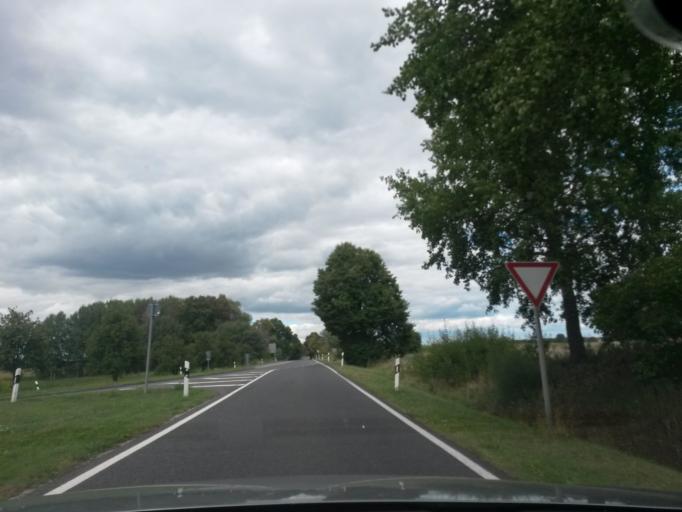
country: DE
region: Brandenburg
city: Angermunde
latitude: 52.9706
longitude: 13.9658
